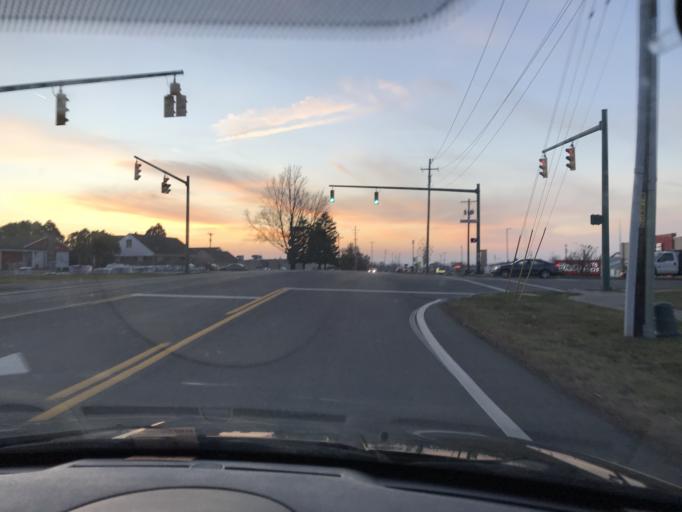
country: US
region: Ohio
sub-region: Champaign County
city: Urbana
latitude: 40.1060
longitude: -83.7174
